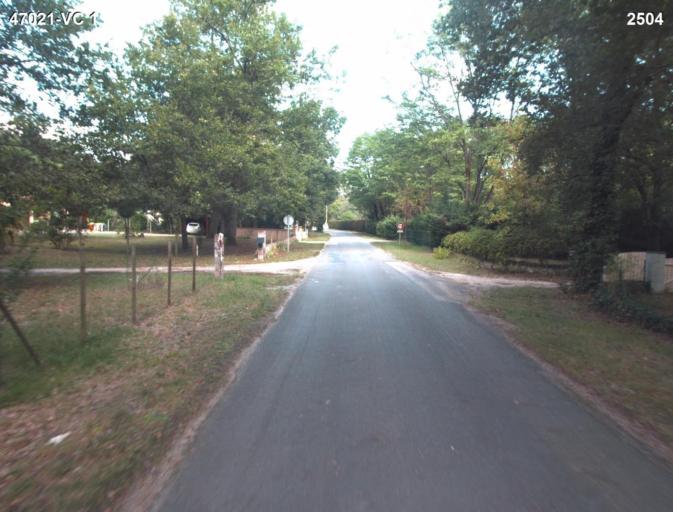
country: FR
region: Aquitaine
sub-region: Departement du Lot-et-Garonne
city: Barbaste
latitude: 44.1454
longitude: 0.2954
